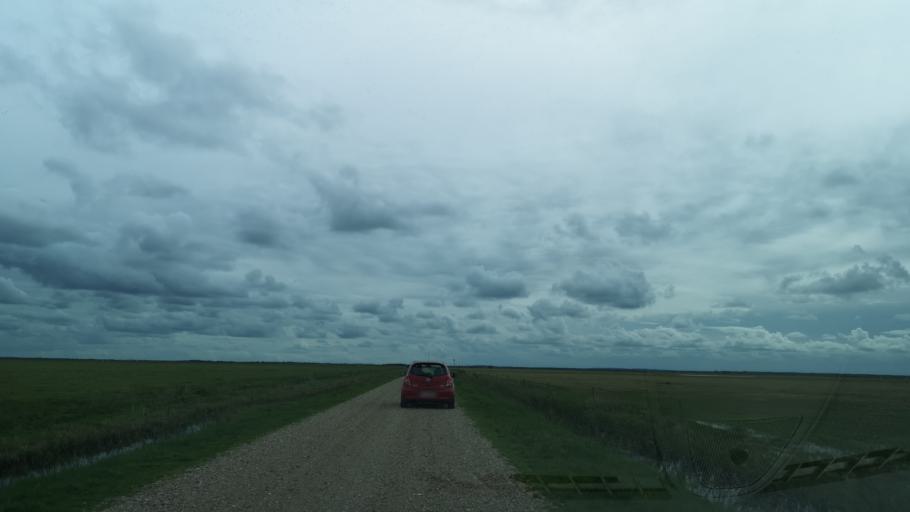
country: DK
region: Central Jutland
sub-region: Ringkobing-Skjern Kommune
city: Hvide Sande
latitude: 55.8849
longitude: 8.2201
